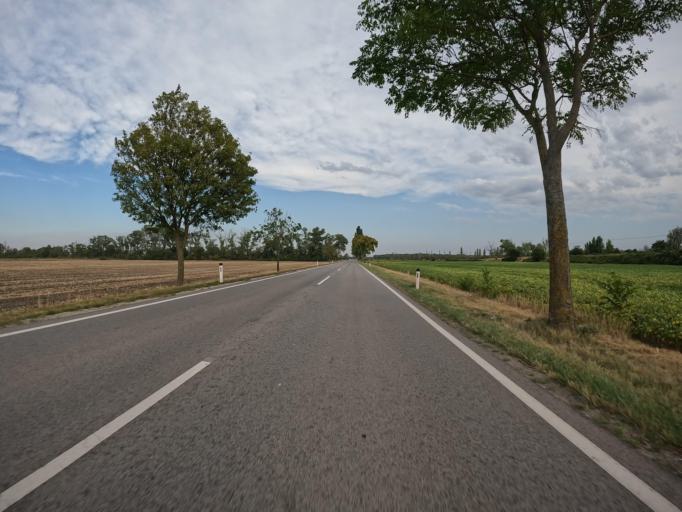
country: AT
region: Lower Austria
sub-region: Politischer Bezirk Baden
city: Traiskirchen
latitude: 48.0048
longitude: 16.3149
